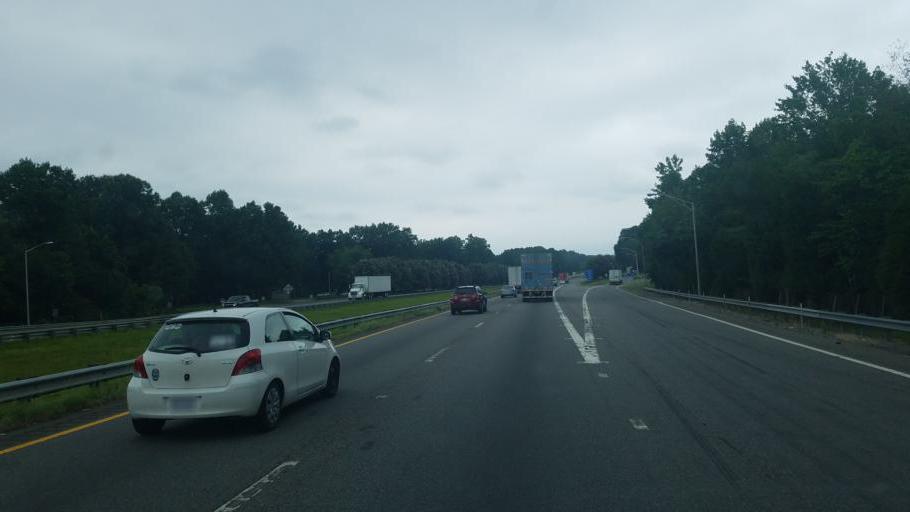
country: US
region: North Carolina
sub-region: Iredell County
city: Mooresville
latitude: 35.6285
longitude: -80.8620
